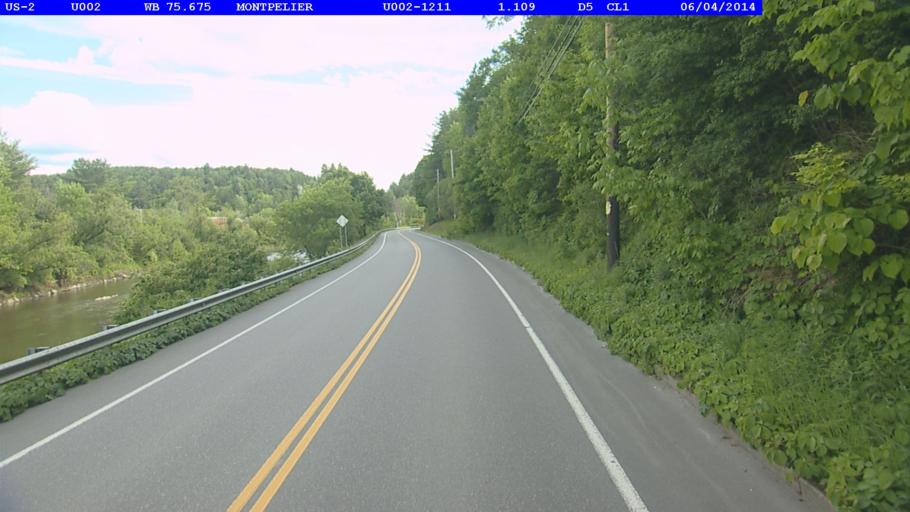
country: US
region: Vermont
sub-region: Washington County
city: Montpelier
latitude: 44.2589
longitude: -72.5927
